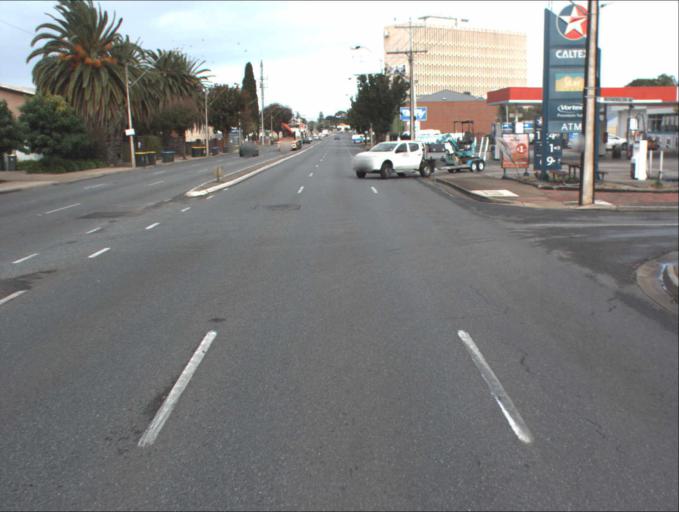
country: AU
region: South Australia
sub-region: Port Adelaide Enfield
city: Klemzig
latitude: -34.8864
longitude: 138.6171
